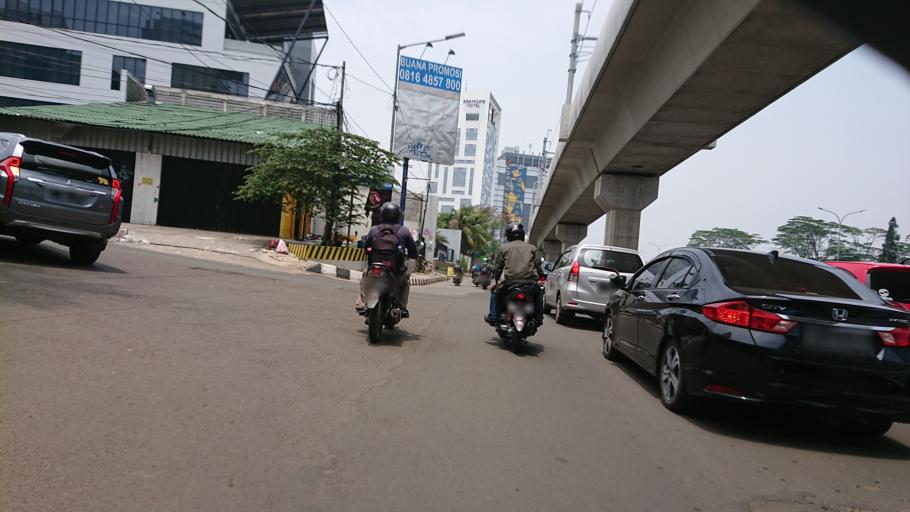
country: ID
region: Banten
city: South Tangerang
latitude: -6.2914
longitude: 106.7824
